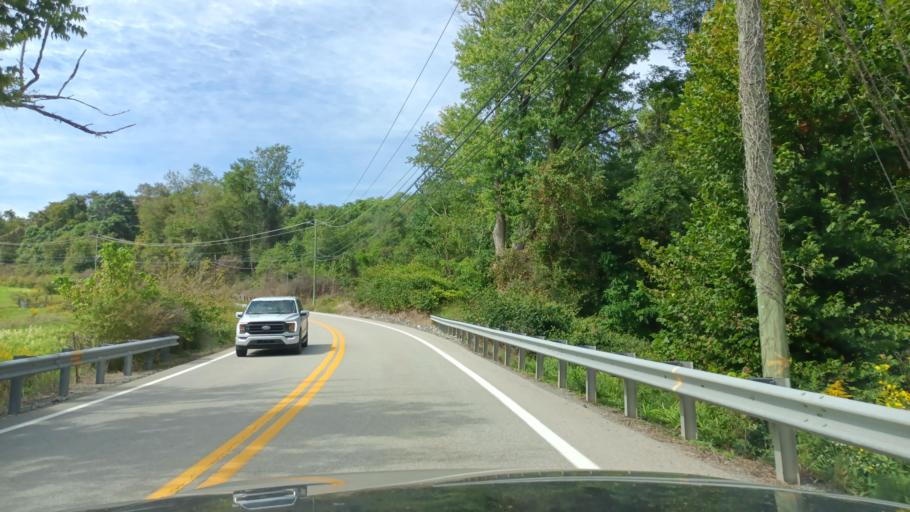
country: US
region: West Virginia
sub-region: Harrison County
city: Bridgeport
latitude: 39.2955
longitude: -80.2130
